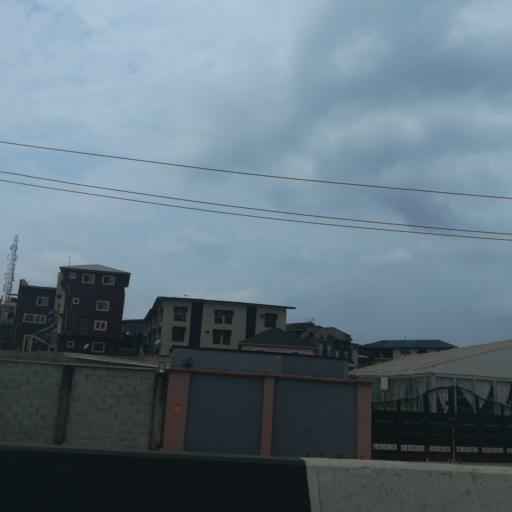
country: NG
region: Lagos
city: Ojota
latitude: 6.5769
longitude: 3.3964
